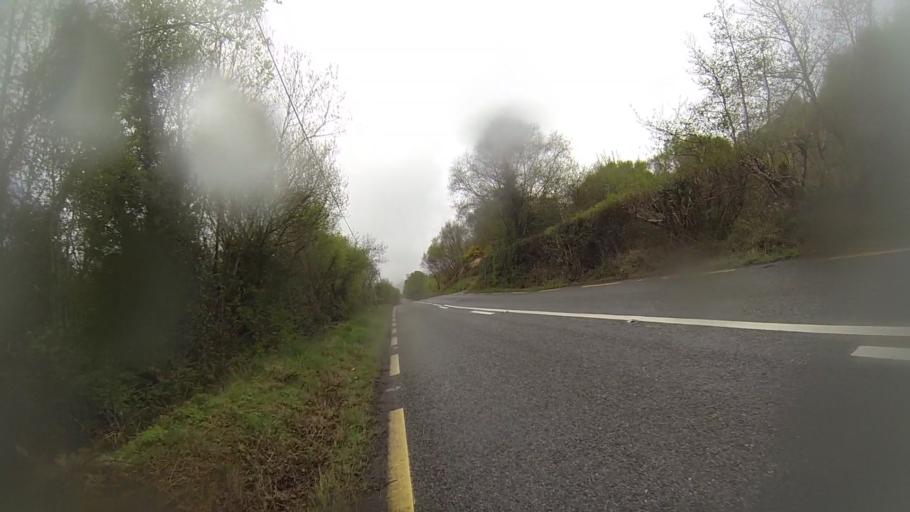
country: IE
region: Munster
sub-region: Ciarrai
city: Kenmare
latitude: 51.8126
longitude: -9.5513
